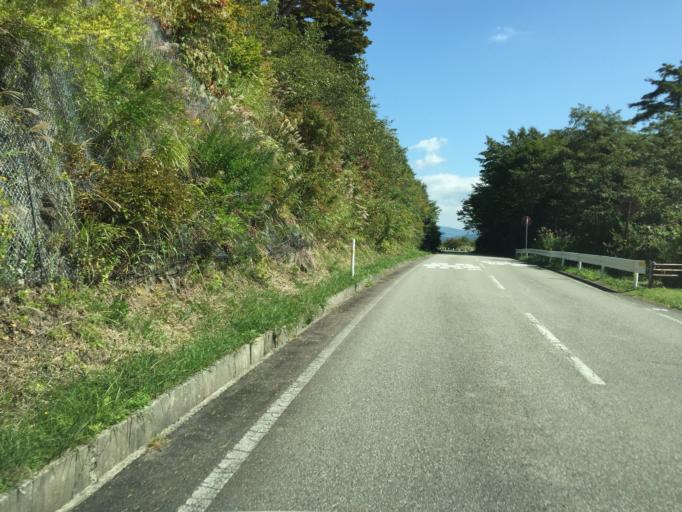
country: JP
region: Fukushima
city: Inawashiro
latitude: 37.6764
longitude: 140.1243
